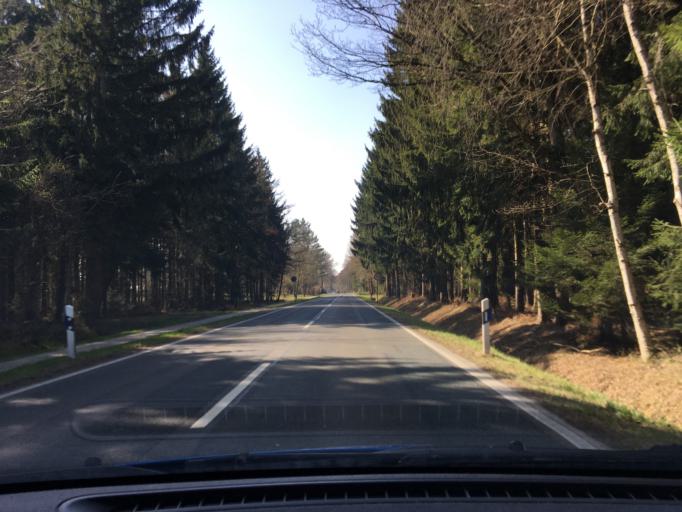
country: DE
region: Lower Saxony
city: Hermannsburg
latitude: 52.8246
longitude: 10.1244
